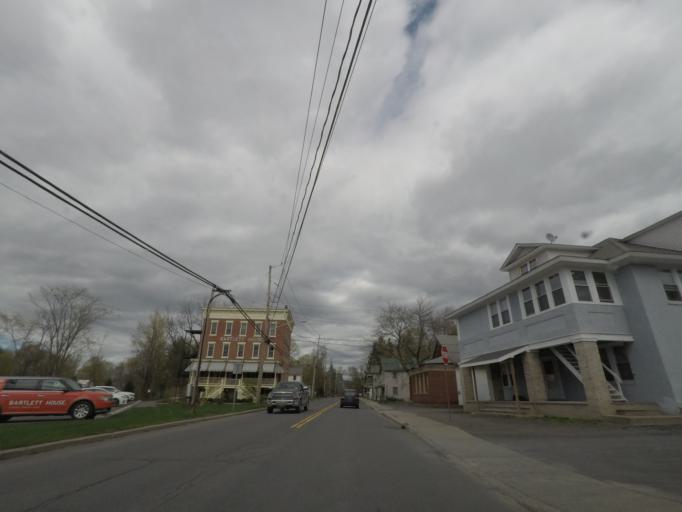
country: US
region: New York
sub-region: Columbia County
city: Chatham
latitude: 42.3268
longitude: -73.6187
